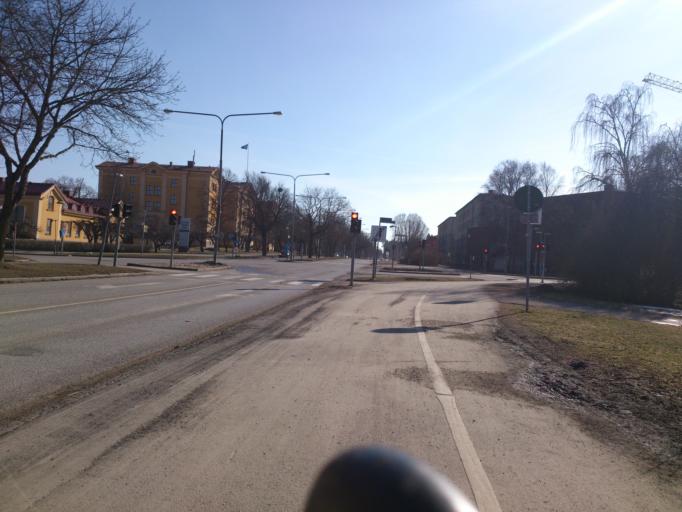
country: SE
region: Uppsala
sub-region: Uppsala Kommun
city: Uppsala
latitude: 59.8466
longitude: 17.6373
